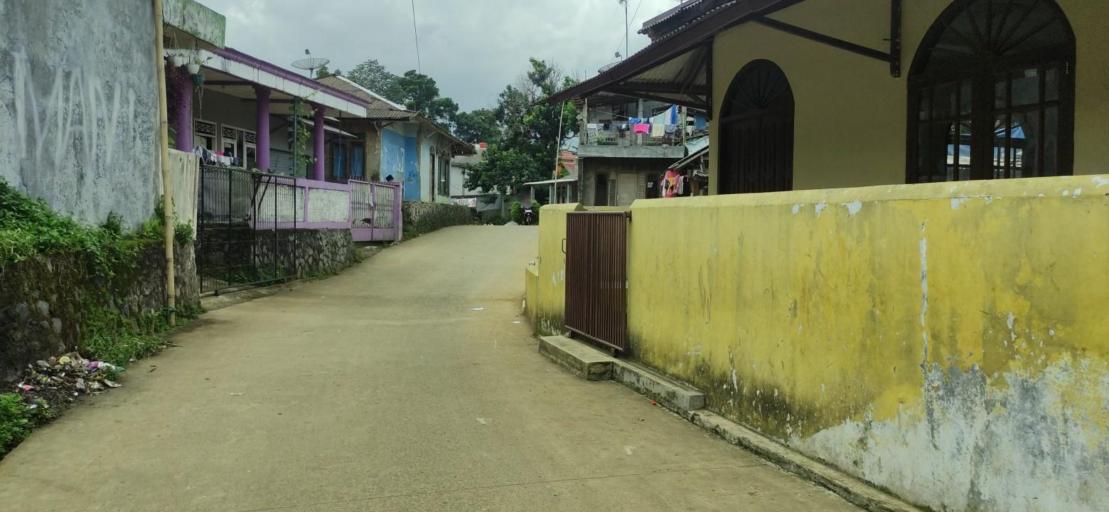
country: ID
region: West Java
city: Caringin
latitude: -6.6430
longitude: 106.8947
